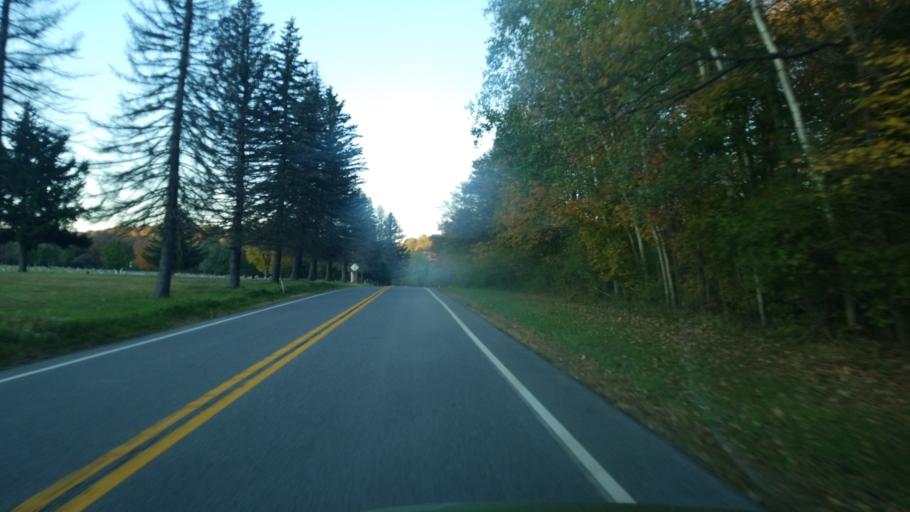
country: US
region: Pennsylvania
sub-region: Jefferson County
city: Reynoldsville
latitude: 41.0761
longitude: -78.9036
